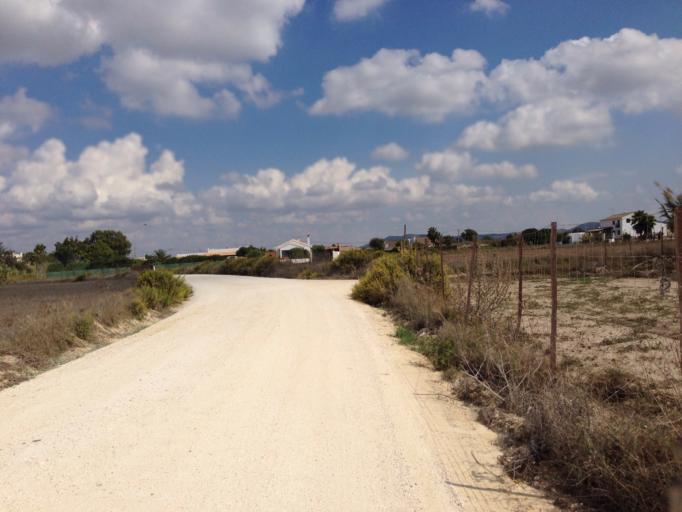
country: ES
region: Andalusia
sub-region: Provincia de Cadiz
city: Conil de la Frontera
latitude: 36.2464
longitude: -6.0722
